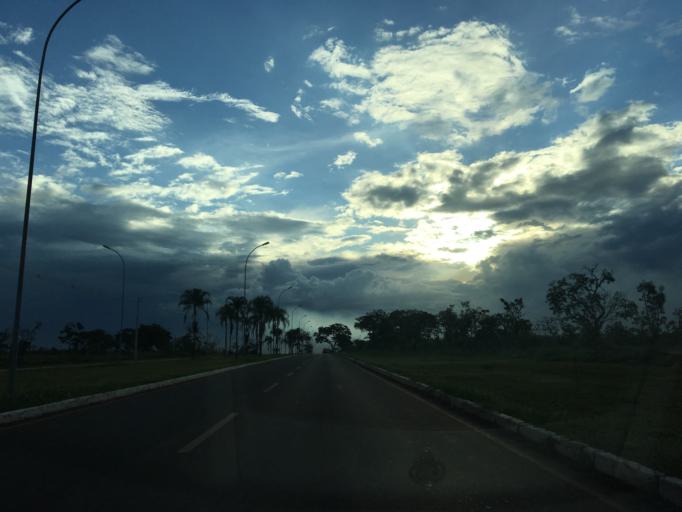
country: BR
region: Federal District
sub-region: Brasilia
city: Brasilia
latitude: -15.8078
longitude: -47.8399
